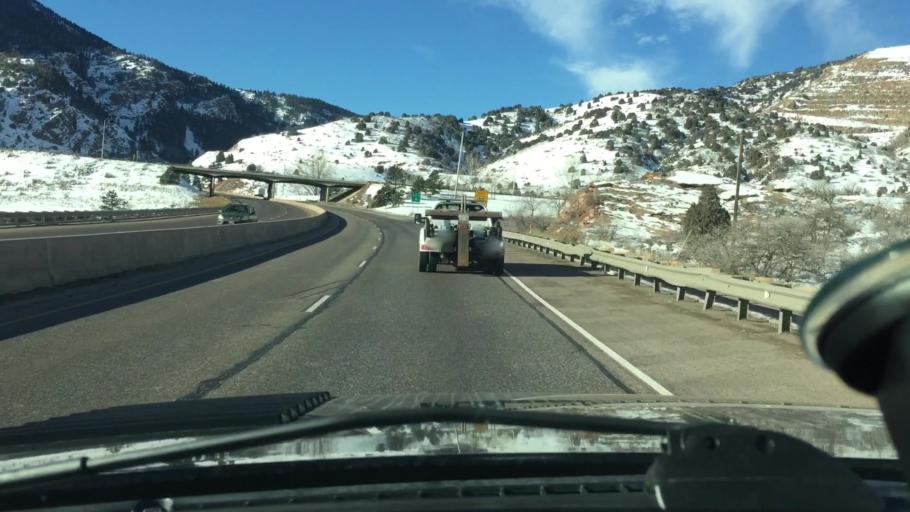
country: US
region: Colorado
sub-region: Jefferson County
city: Indian Hills
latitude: 39.6254
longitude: -105.1899
